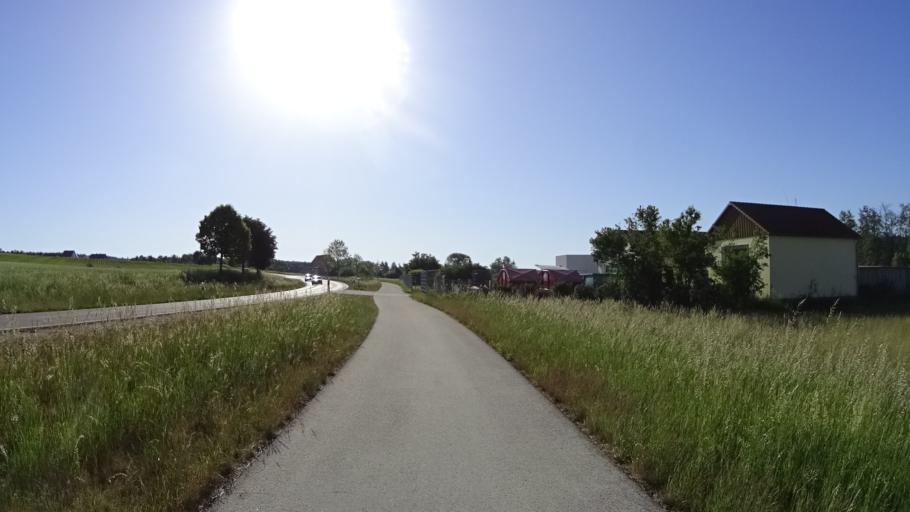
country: DE
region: Bavaria
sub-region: Regierungsbezirk Mittelfranken
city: Wieseth
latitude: 49.1605
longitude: 10.4959
